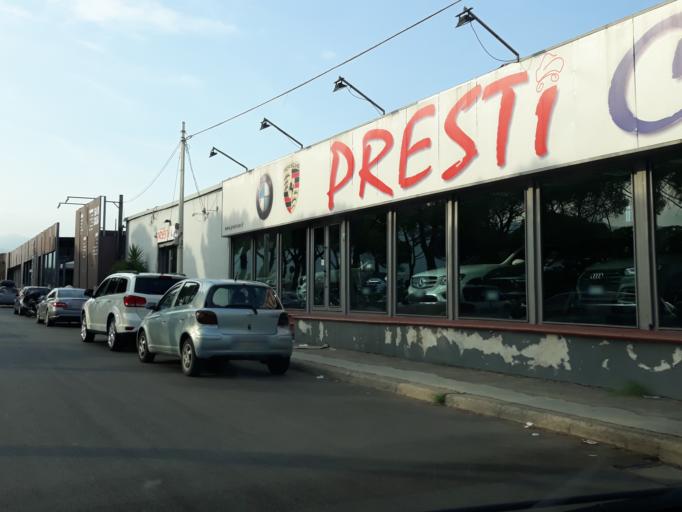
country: IT
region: Sicily
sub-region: Palermo
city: Villa Ciambra
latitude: 38.0889
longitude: 13.3463
